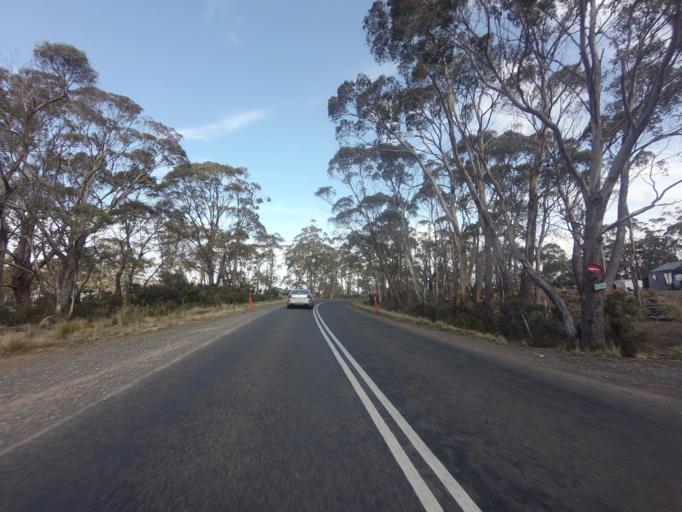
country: AU
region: Tasmania
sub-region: Meander Valley
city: Deloraine
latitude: -41.7911
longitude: 146.6933
